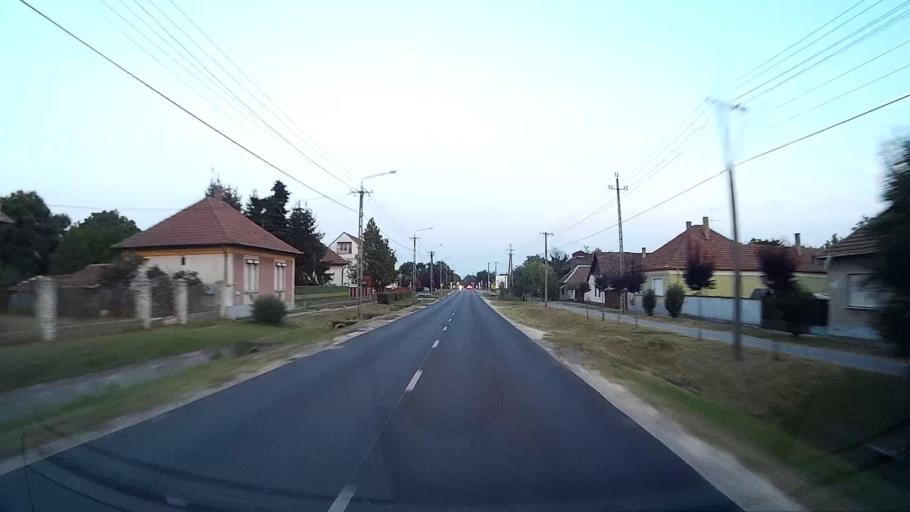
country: HU
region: Pest
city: Cegledbercel
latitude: 47.2134
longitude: 19.6785
